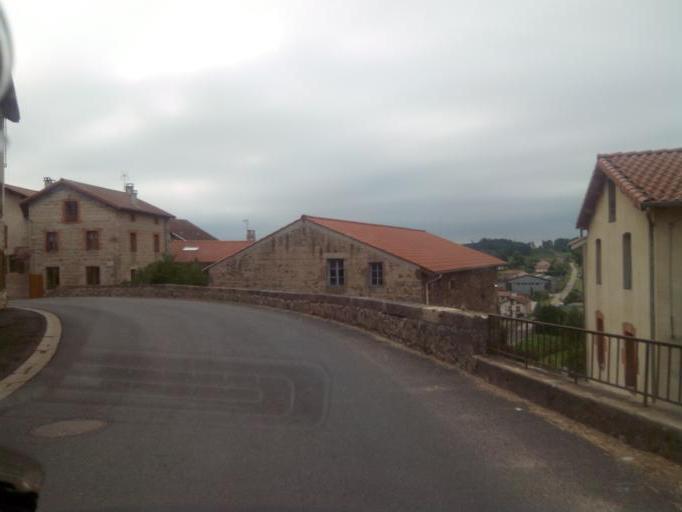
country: FR
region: Rhone-Alpes
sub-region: Departement de la Loire
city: Usson-en-Forez
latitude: 45.3571
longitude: 3.9559
